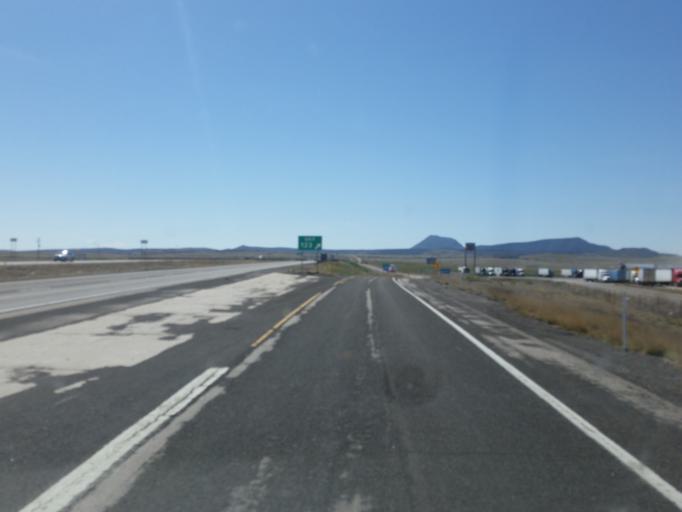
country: US
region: Arizona
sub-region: Yavapai County
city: Paulden
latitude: 35.3116
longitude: -112.8587
